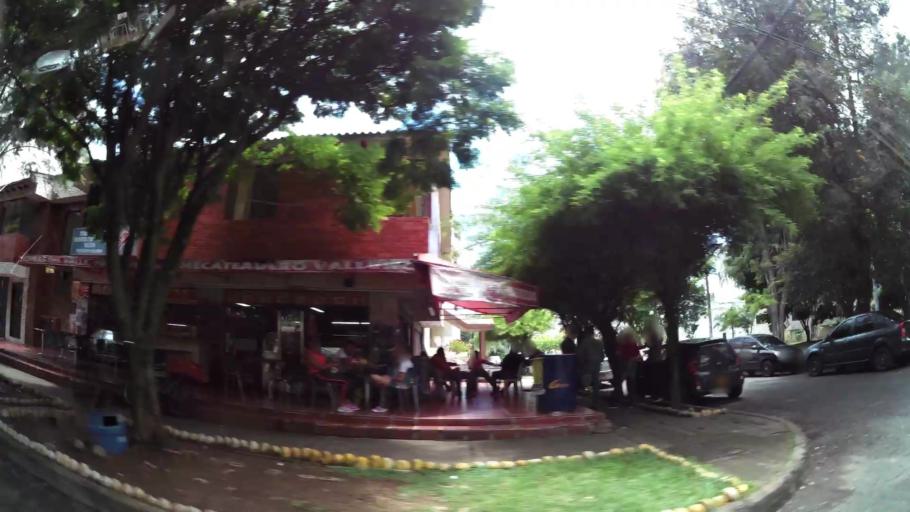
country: CO
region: Valle del Cauca
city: Cali
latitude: 3.3831
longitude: -76.5303
